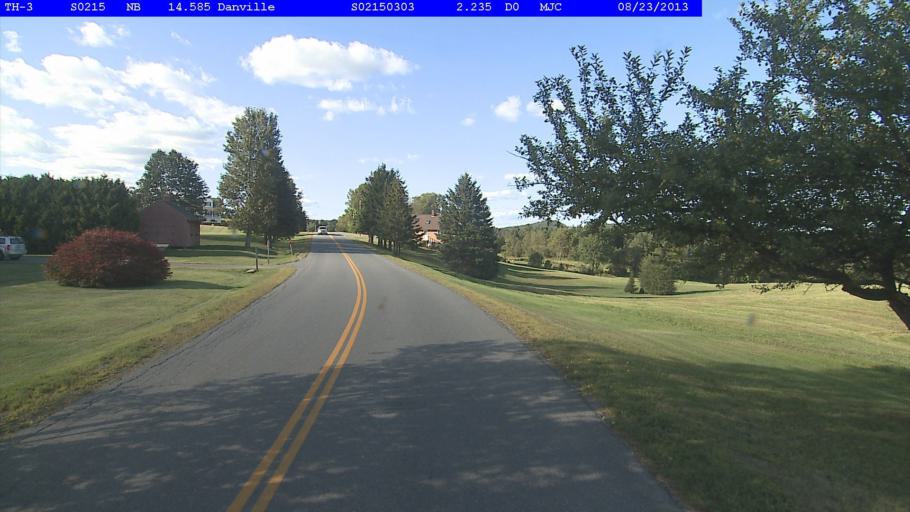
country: US
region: Vermont
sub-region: Caledonia County
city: Saint Johnsbury
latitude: 44.3970
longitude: -72.1398
